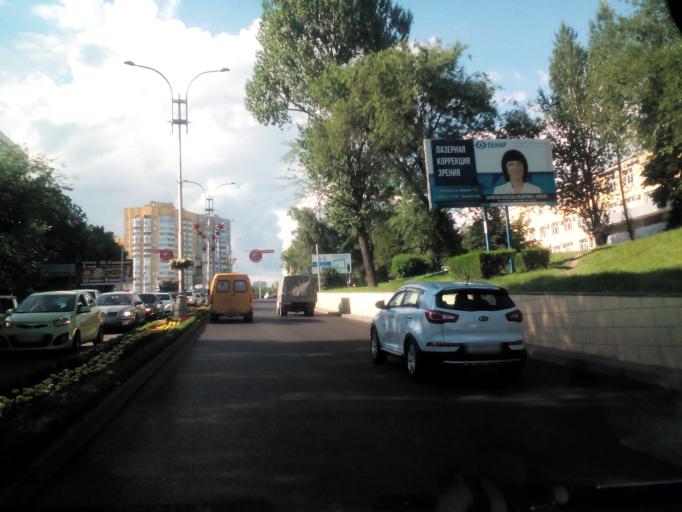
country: RU
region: Stavropol'skiy
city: Pyatigorsk
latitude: 44.0516
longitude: 43.0650
